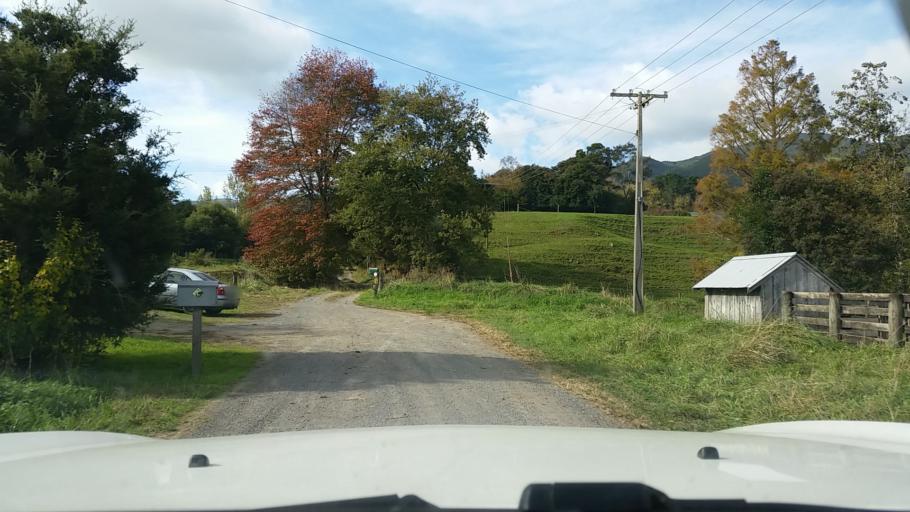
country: NZ
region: Waikato
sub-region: Hauraki District
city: Paeroa
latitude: -37.5102
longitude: 175.7011
